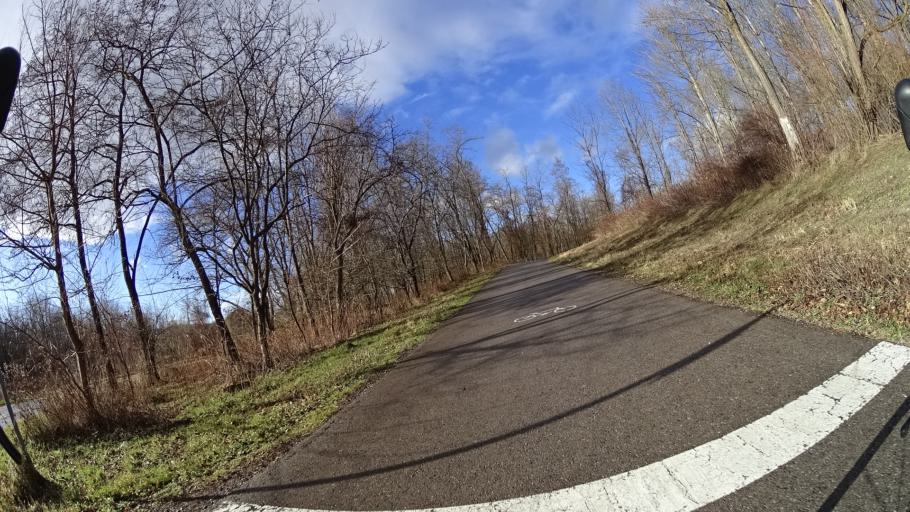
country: AT
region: Lower Austria
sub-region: Politischer Bezirk Tulln
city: Fels am Wagram
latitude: 48.3707
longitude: 15.8475
